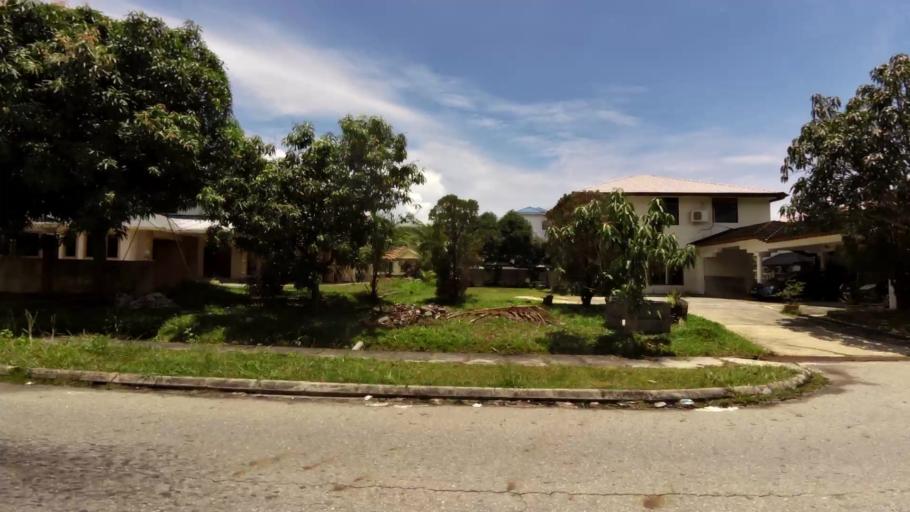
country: BN
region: Brunei and Muara
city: Bandar Seri Begawan
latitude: 4.9658
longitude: 114.9199
